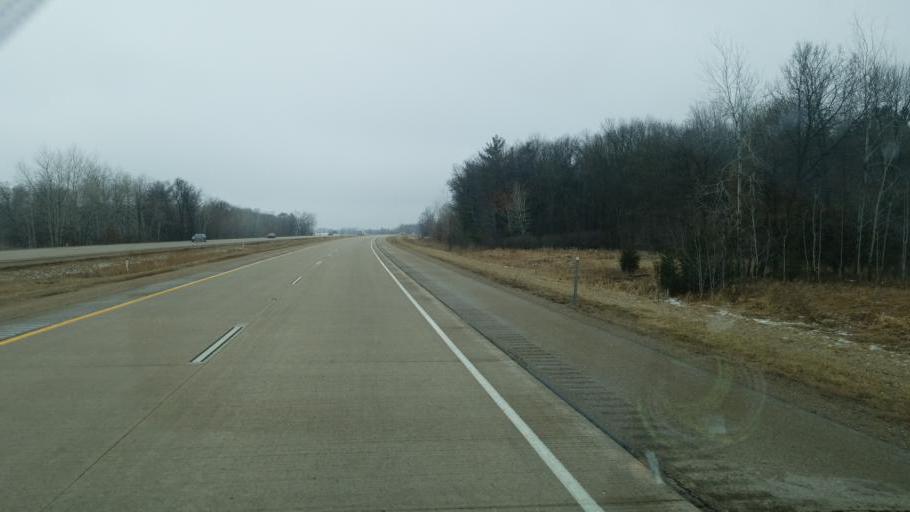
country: US
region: Wisconsin
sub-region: Waupaca County
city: Weyauwega
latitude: 44.2512
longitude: -88.8288
